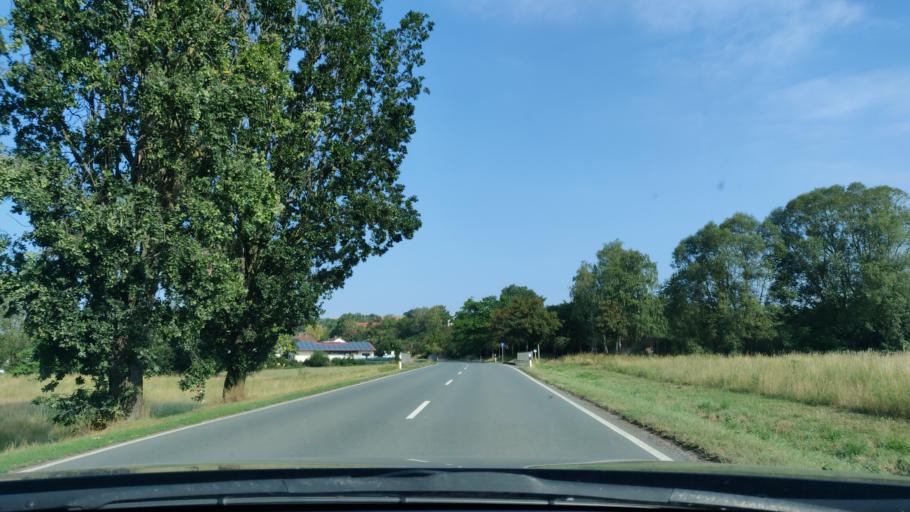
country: DE
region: Hesse
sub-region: Regierungsbezirk Kassel
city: Bad Wildungen
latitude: 51.1634
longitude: 9.1447
